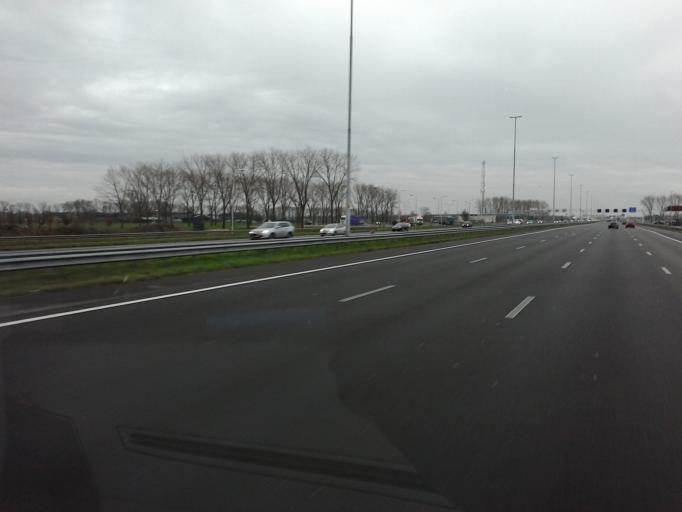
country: NL
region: Gelderland
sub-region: Gemeente Culemborg
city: Culemborg
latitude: 51.9146
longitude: 5.1776
